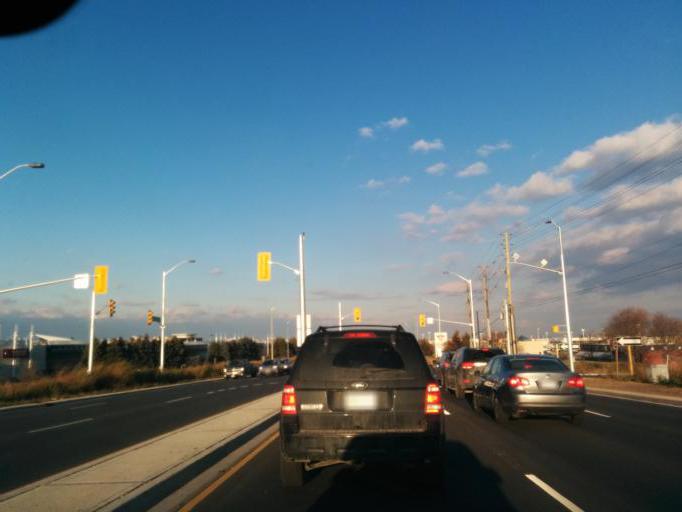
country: CA
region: Ontario
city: Oakville
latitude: 43.5129
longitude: -79.6922
